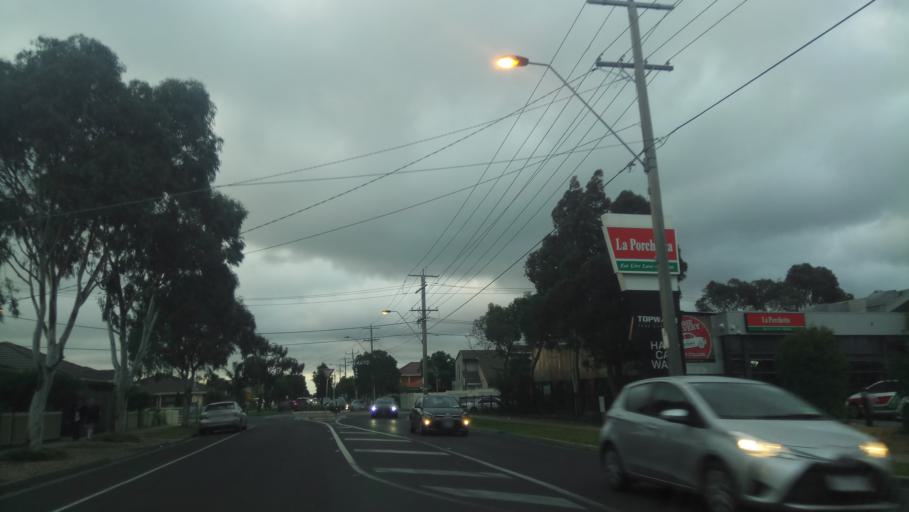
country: AU
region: Victoria
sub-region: Hobsons Bay
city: Altona Meadows
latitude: -37.8736
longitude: 144.7773
